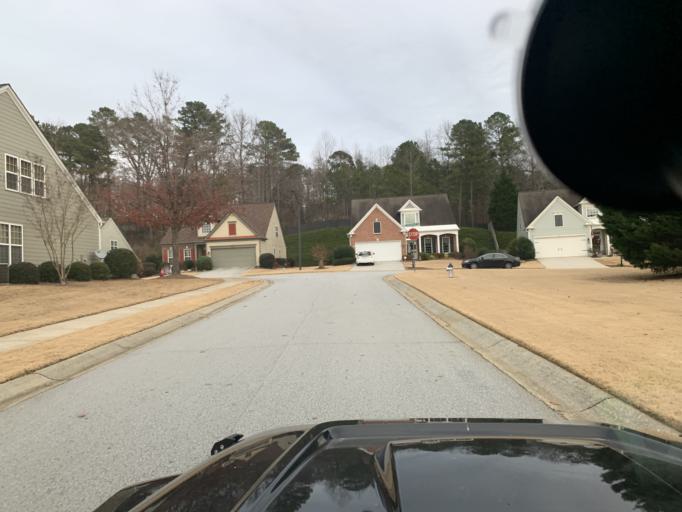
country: US
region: Georgia
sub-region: Cherokee County
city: Woodstock
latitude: 34.0875
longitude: -84.4549
